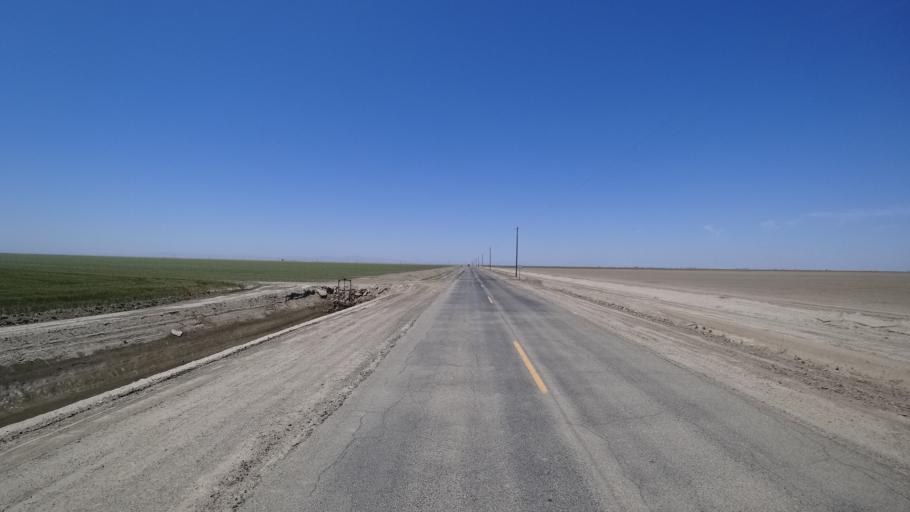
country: US
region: California
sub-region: Kings County
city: Corcoran
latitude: 36.1162
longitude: -119.6620
